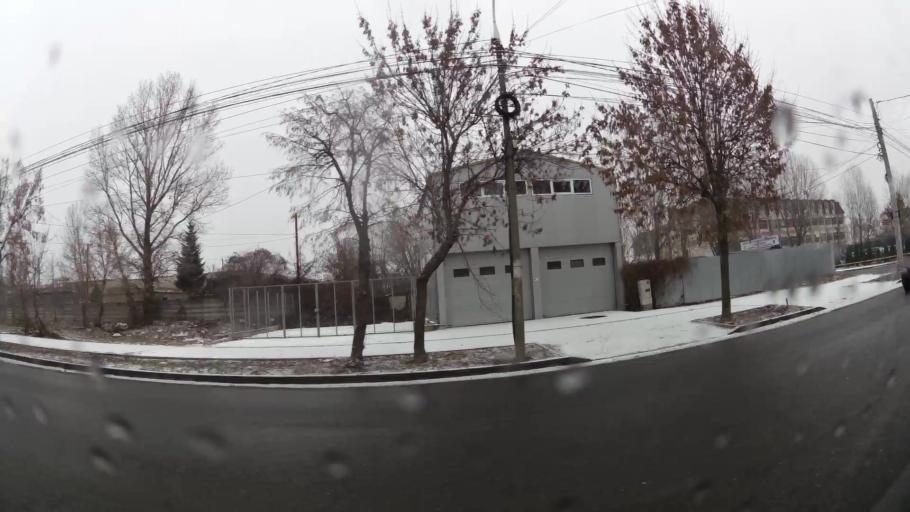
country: RO
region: Dambovita
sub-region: Municipiul Targoviste
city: Targoviste
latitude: 44.9126
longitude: 25.4449
